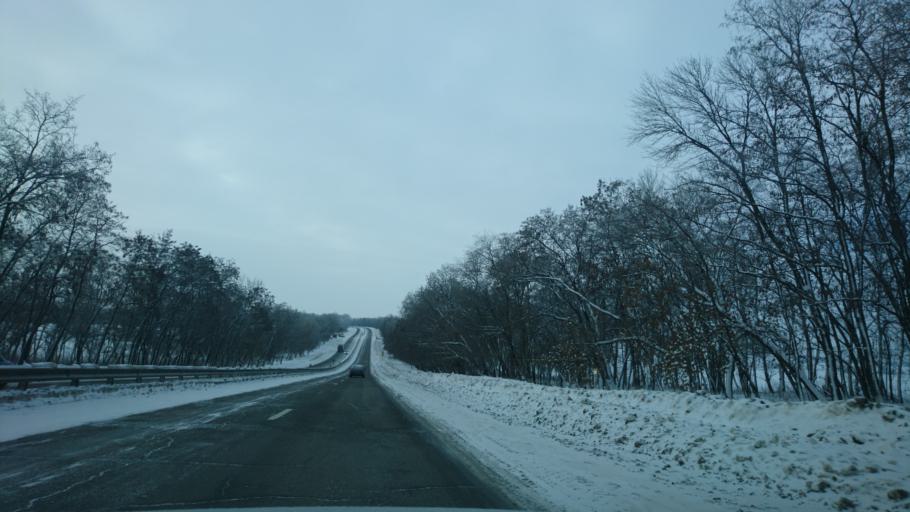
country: RU
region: Belgorod
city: Mayskiy
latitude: 50.4884
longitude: 36.4155
